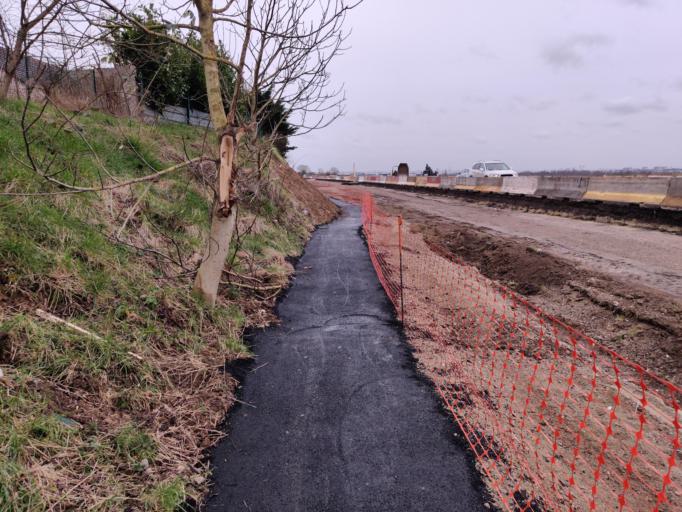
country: FR
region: Ile-de-France
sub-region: Departement du Val-d'Oise
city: Fontenay-en-Parisis
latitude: 49.0307
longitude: 2.4475
